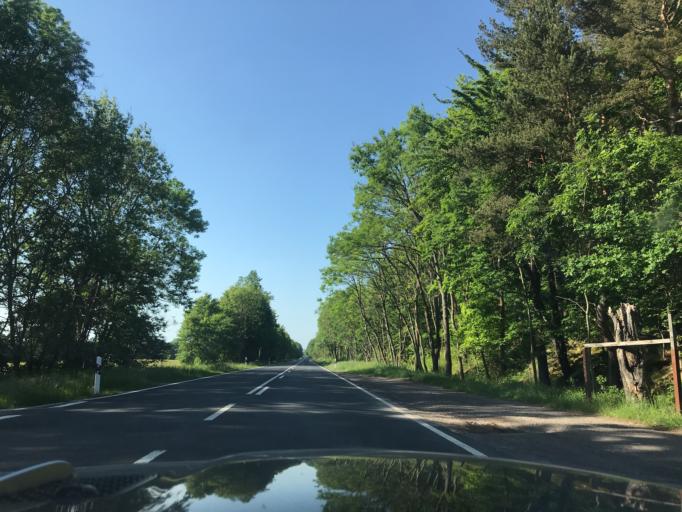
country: DE
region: Thuringia
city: Luisenthal
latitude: 50.7970
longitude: 10.7489
